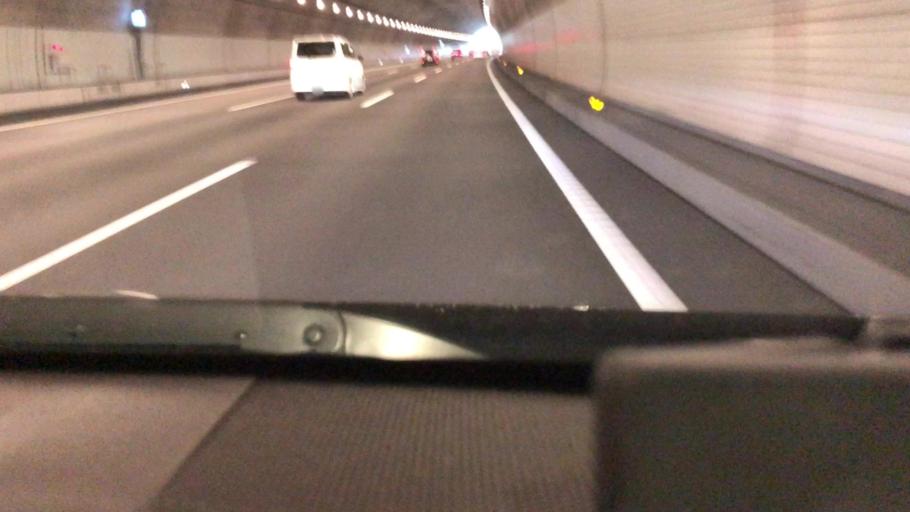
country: JP
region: Shizuoka
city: Shizuoka-shi
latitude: 34.9981
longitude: 138.3031
